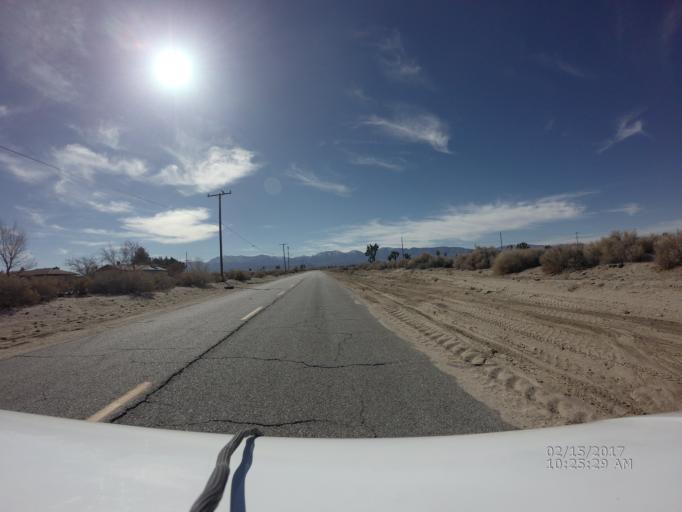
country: US
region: California
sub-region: Los Angeles County
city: Lake Los Angeles
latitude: 34.5816
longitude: -117.8623
